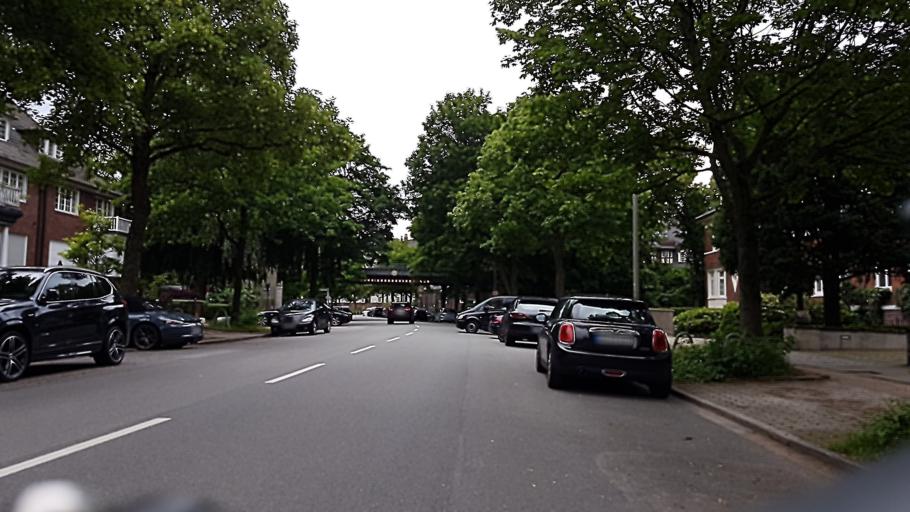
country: DE
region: Hamburg
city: Winterhude
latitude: 53.5895
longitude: 9.9958
